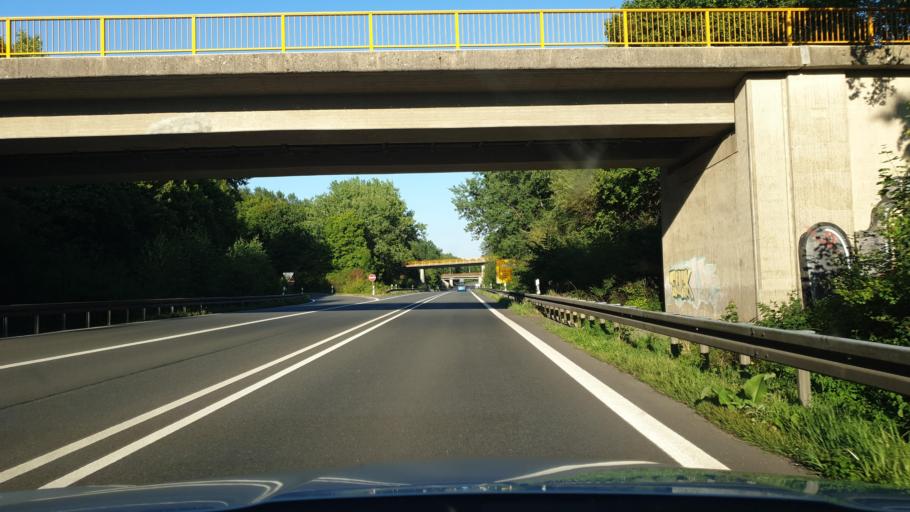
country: DE
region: Lower Saxony
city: Buckeburg
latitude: 52.2709
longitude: 9.0514
